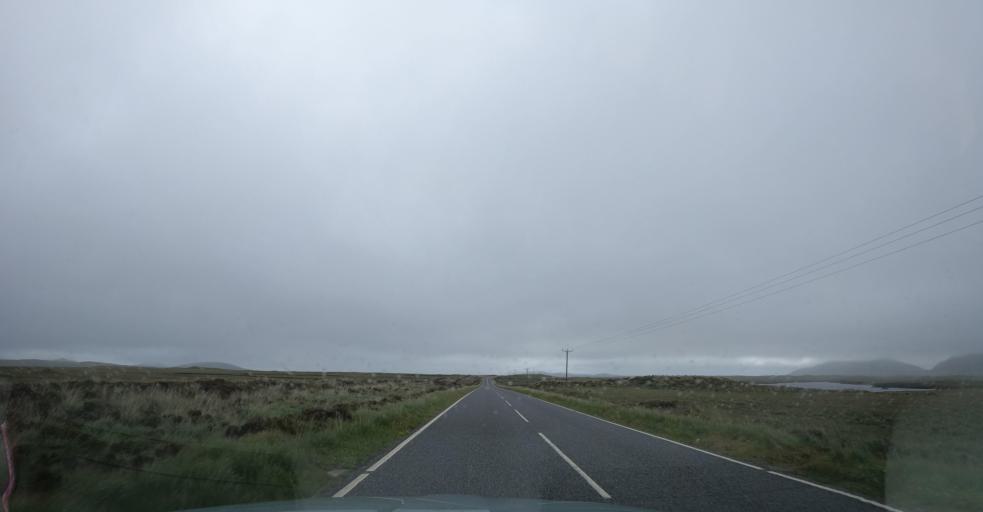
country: GB
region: Scotland
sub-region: Eilean Siar
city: Isle of North Uist
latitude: 57.5887
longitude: -7.2278
